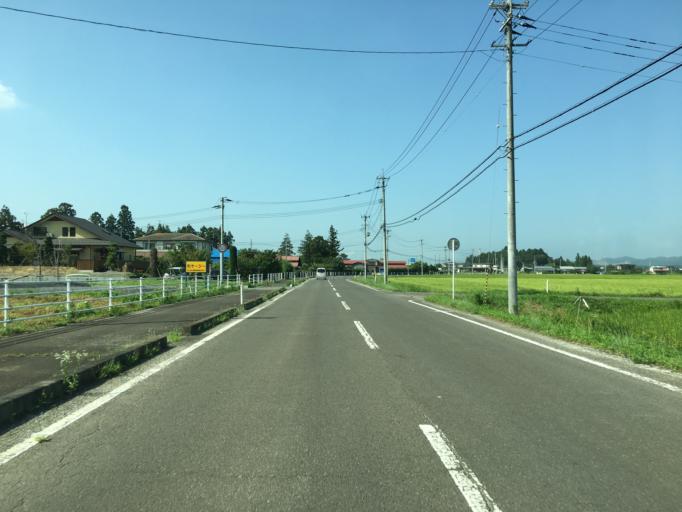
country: JP
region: Miyagi
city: Kakuda
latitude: 37.9537
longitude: 140.7955
